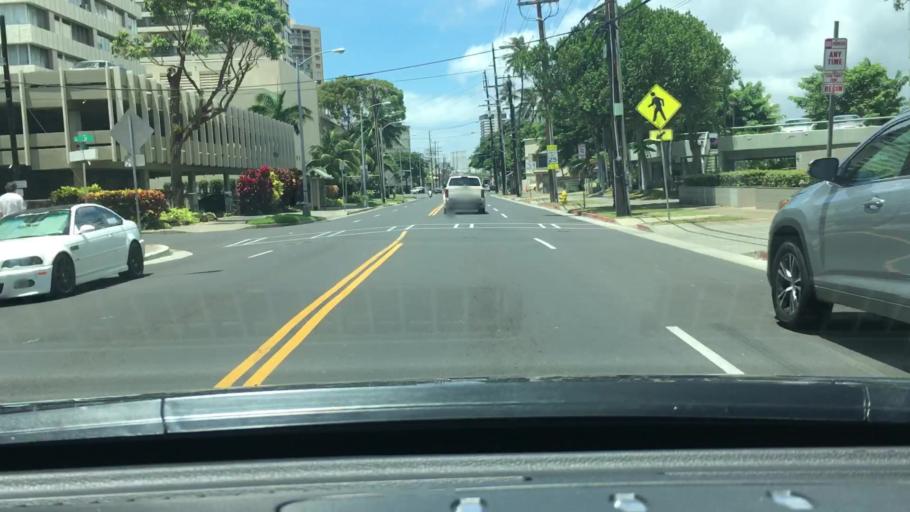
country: US
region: Hawaii
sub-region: Honolulu County
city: Honolulu
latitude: 21.2863
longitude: -157.8223
